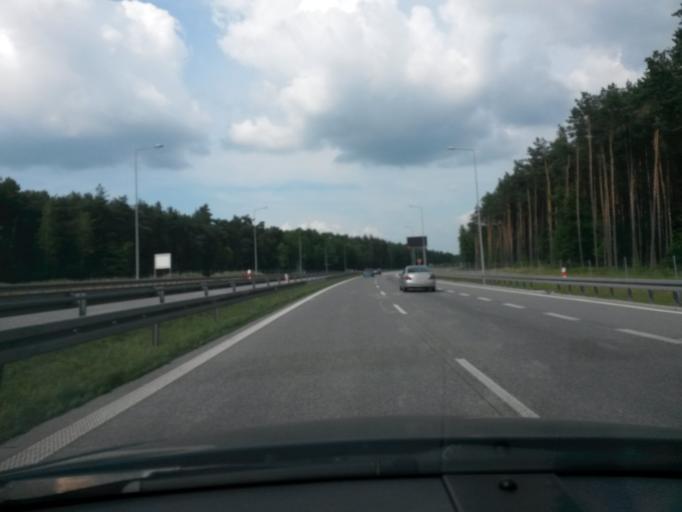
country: PL
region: Lodz Voivodeship
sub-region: Powiat tomaszowski
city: Lubochnia
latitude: 51.6266
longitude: 20.0982
